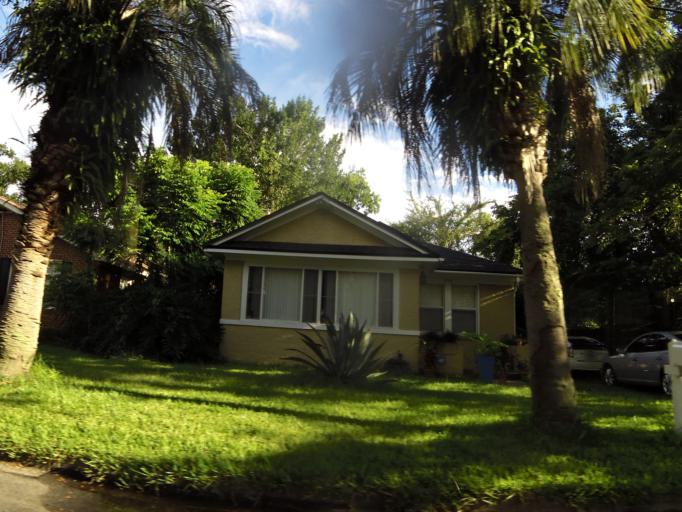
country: US
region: Florida
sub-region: Duval County
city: Jacksonville
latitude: 30.3099
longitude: -81.7267
